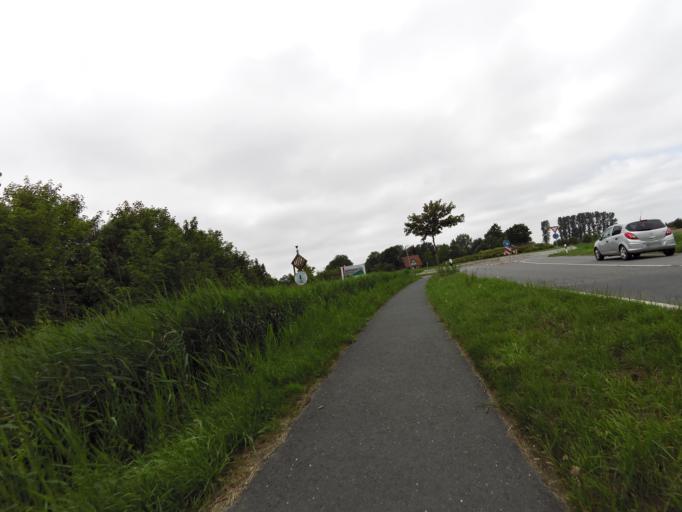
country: DE
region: Lower Saxony
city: Dorum
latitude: 53.6963
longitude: 8.5624
